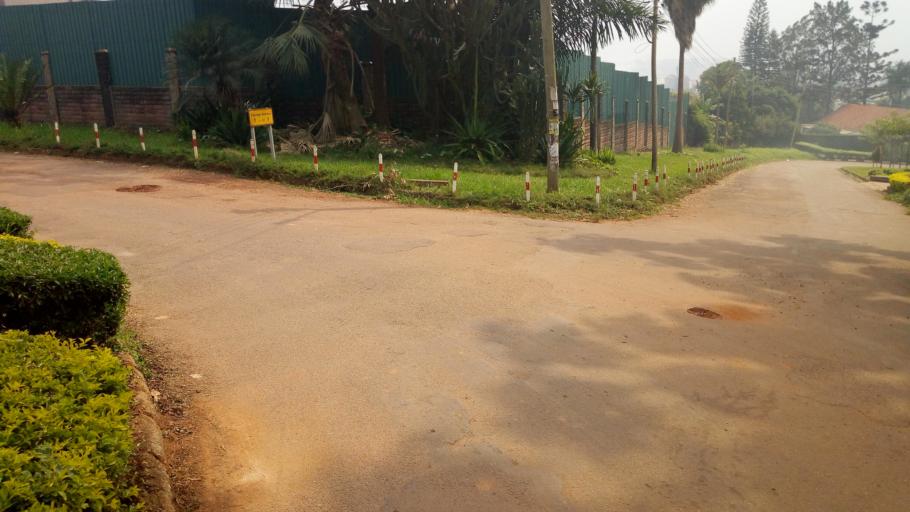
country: UG
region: Central Region
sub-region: Kampala District
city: Kampala
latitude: 0.3149
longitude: 32.6191
